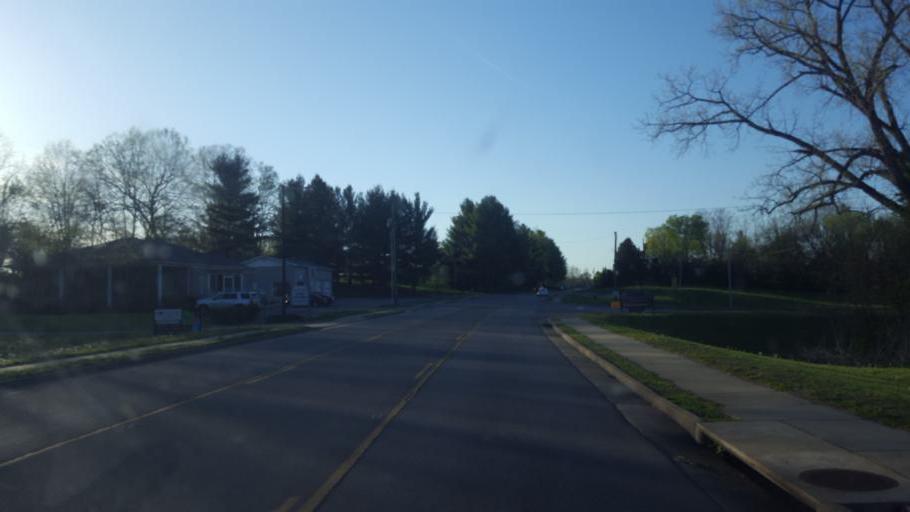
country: US
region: Kentucky
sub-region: Hart County
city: Munfordville
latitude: 37.2751
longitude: -85.8958
